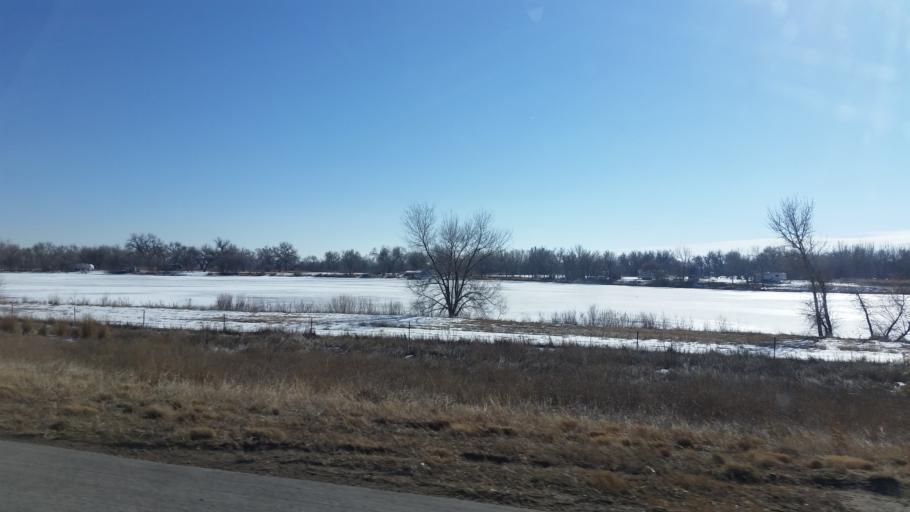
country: US
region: Colorado
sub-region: Weld County
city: Evans
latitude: 40.3933
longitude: -104.6606
